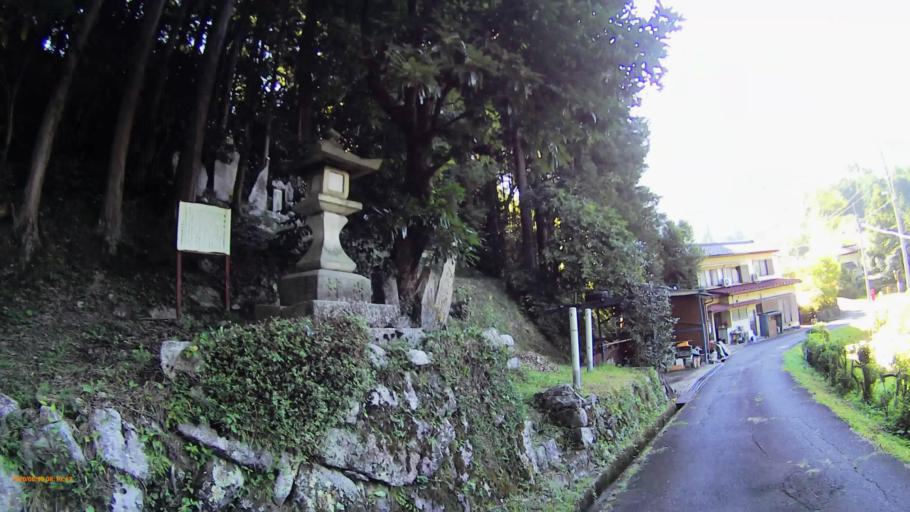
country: JP
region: Nagano
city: Iida
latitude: 35.7302
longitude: 137.7137
